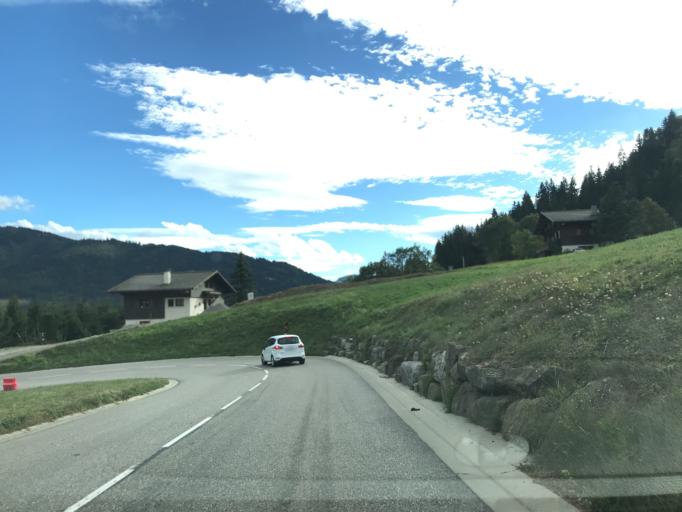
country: FR
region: Rhone-Alpes
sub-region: Departement de la Haute-Savoie
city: Le Grand-Bornand
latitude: 45.9557
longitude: 6.4373
